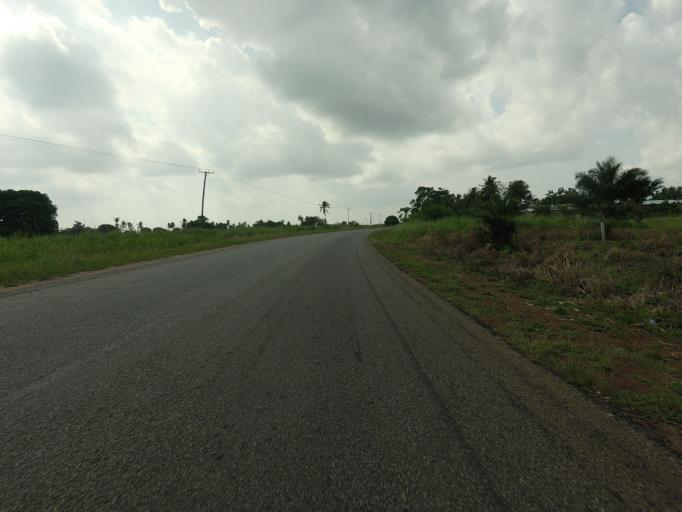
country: GH
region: Volta
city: Ho
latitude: 6.4292
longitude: 0.7323
